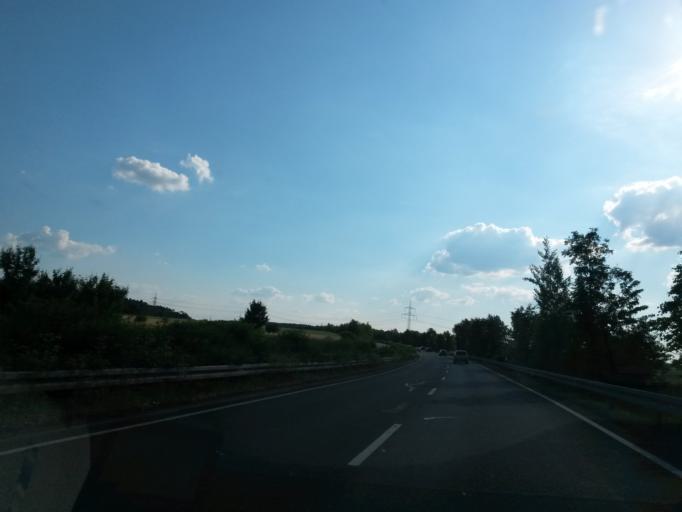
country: DE
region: Bavaria
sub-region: Regierungsbezirk Mittelfranken
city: Puschendorf
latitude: 49.4896
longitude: 10.8389
